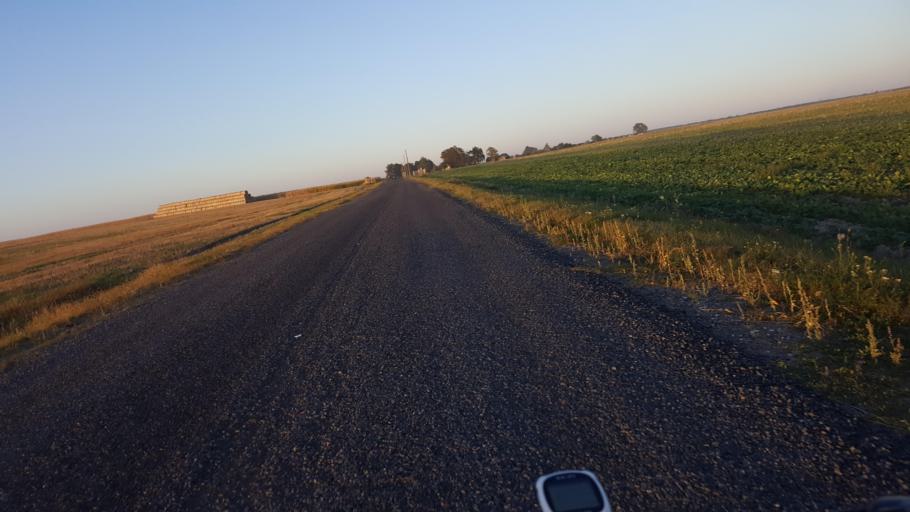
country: BY
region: Brest
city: Charnawchytsy
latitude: 52.2904
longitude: 23.5844
